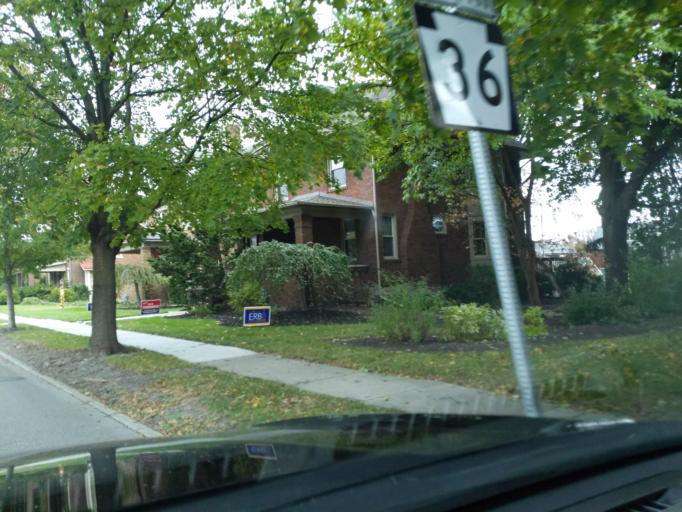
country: US
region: Pennsylvania
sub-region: Blair County
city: Hollidaysburg
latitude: 40.4335
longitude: -78.3914
